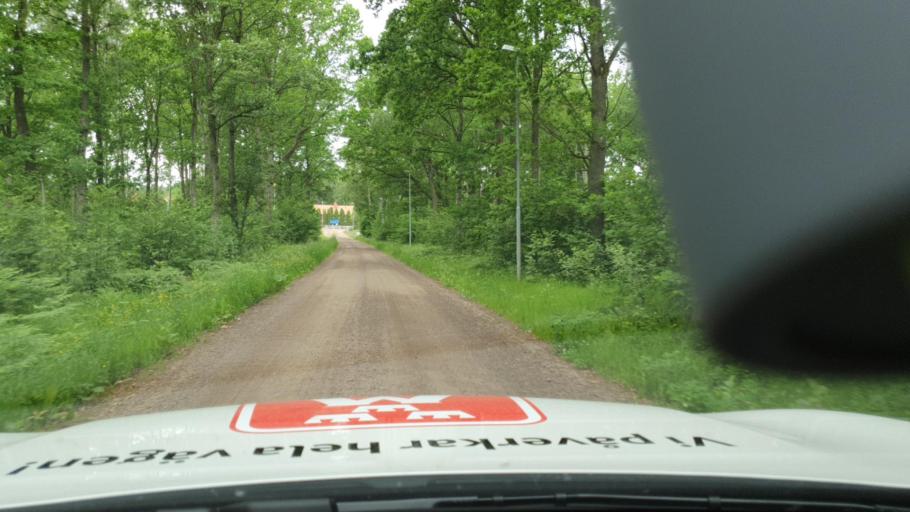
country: SE
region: Vaestra Goetaland
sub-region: Hjo Kommun
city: Hjo
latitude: 58.3536
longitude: 14.3397
